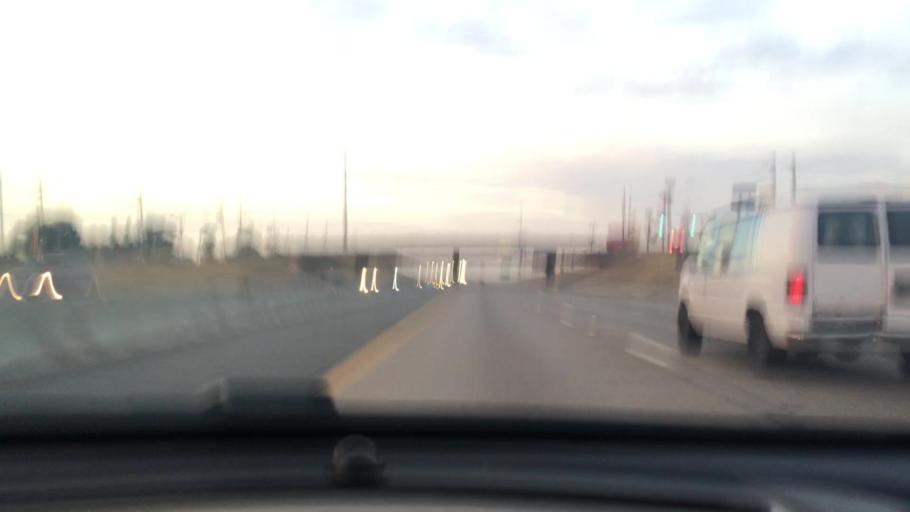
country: US
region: Texas
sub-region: Dallas County
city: Cockrell Hill
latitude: 32.6763
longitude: -96.8226
